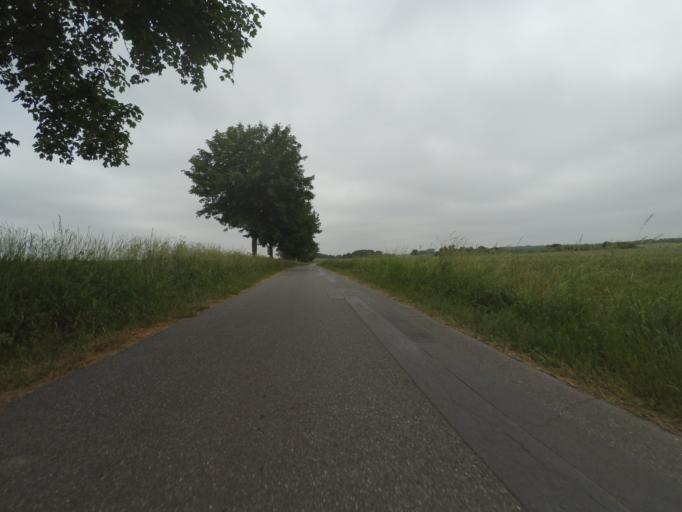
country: DE
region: Mecklenburg-Vorpommern
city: Plau am See
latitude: 53.5001
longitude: 12.1967
